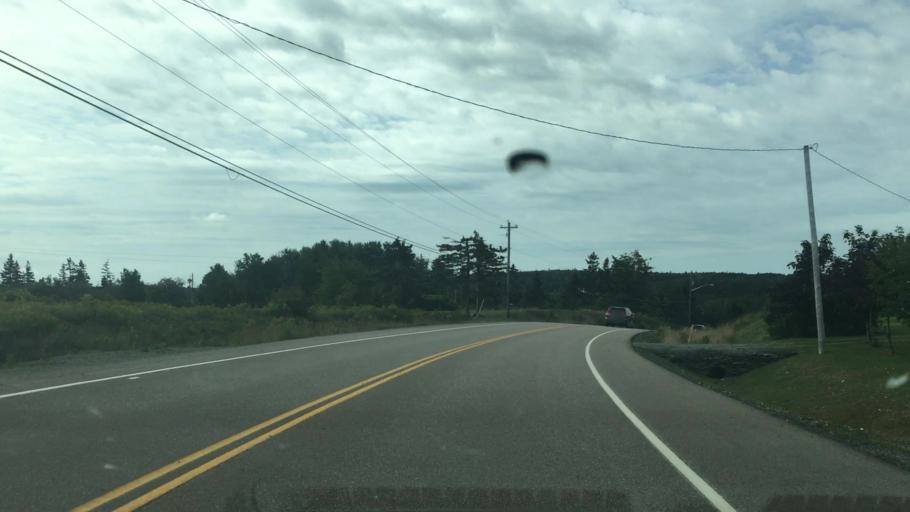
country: CA
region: Nova Scotia
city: Princeville
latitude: 45.6952
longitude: -60.7367
